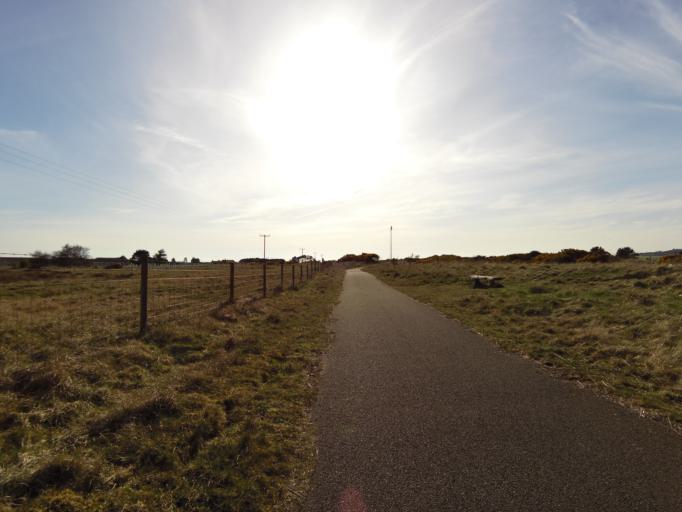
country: GB
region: Scotland
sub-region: Angus
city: Carnoustie
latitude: 56.4873
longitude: -2.7760
